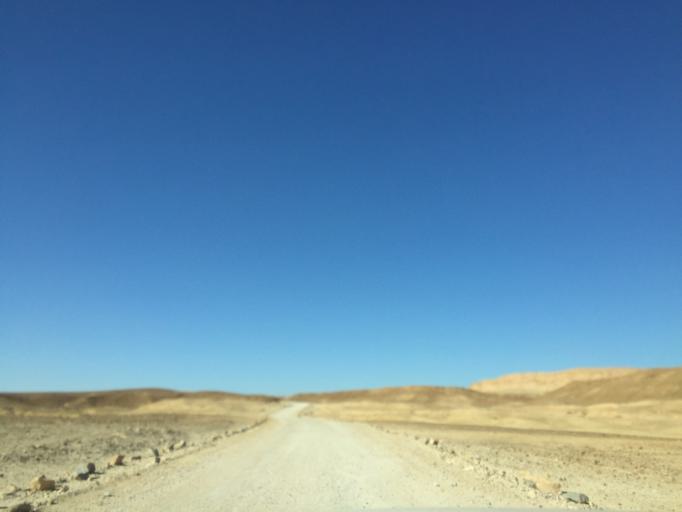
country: IL
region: Southern District
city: Mitzpe Ramon
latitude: 30.6106
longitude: 34.9356
